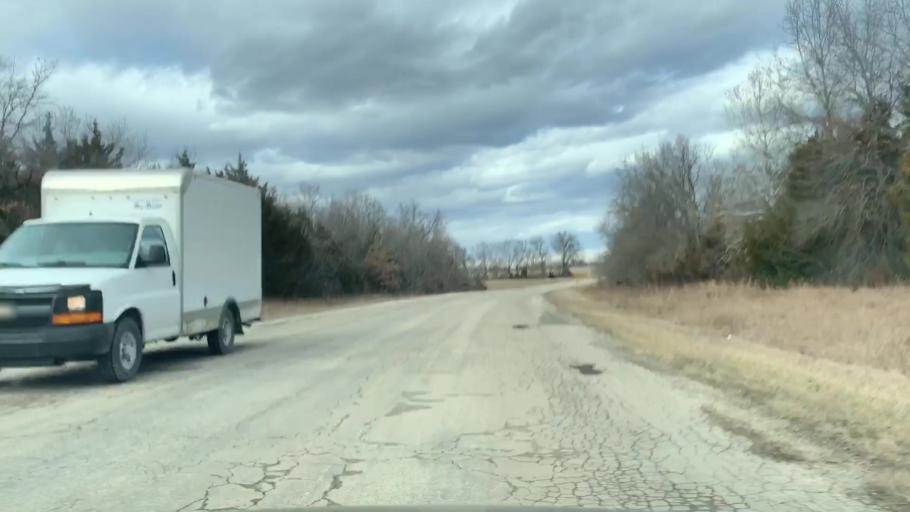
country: US
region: Kansas
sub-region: Allen County
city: Humboldt
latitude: 37.7559
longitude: -95.4718
